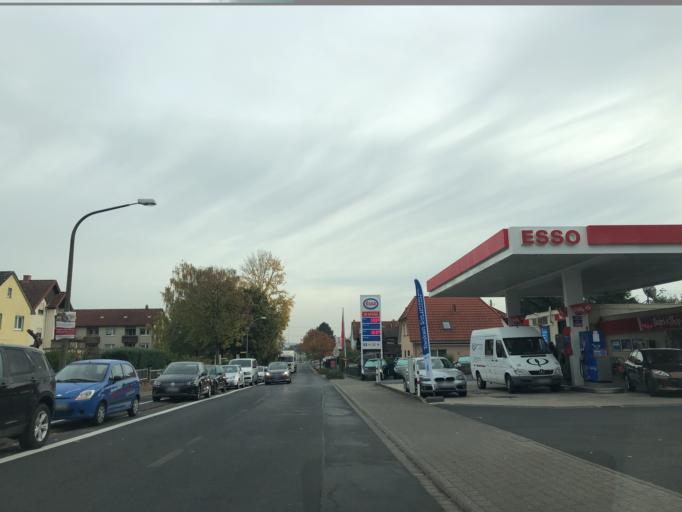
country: DE
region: Hesse
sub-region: Regierungsbezirk Darmstadt
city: Niederdorfelden
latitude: 50.1937
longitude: 8.8083
